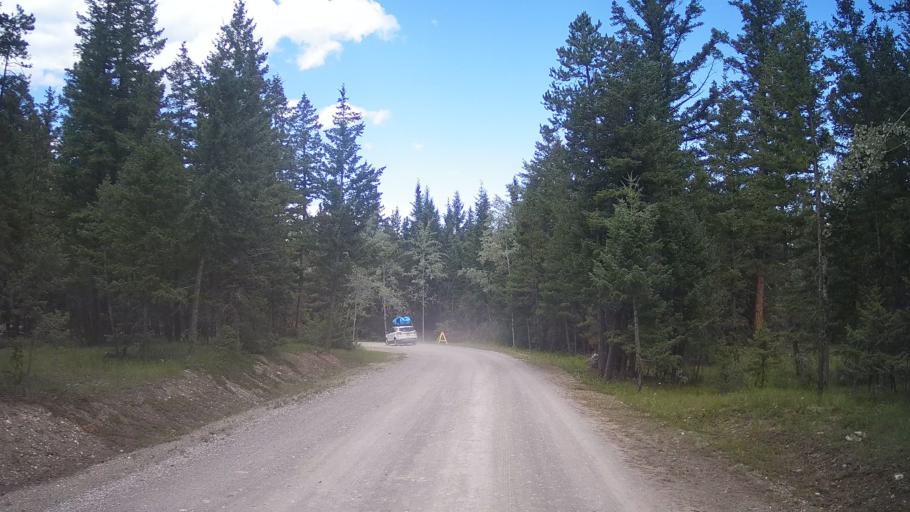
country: CA
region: British Columbia
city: Lillooet
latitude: 51.3107
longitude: -121.8240
